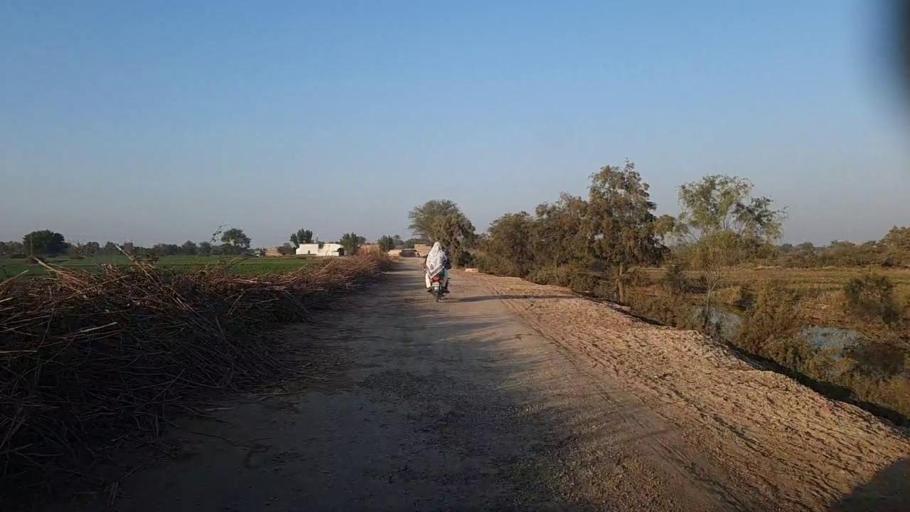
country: PK
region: Sindh
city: Mirpur Mathelo
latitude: 27.8774
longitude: 69.6493
